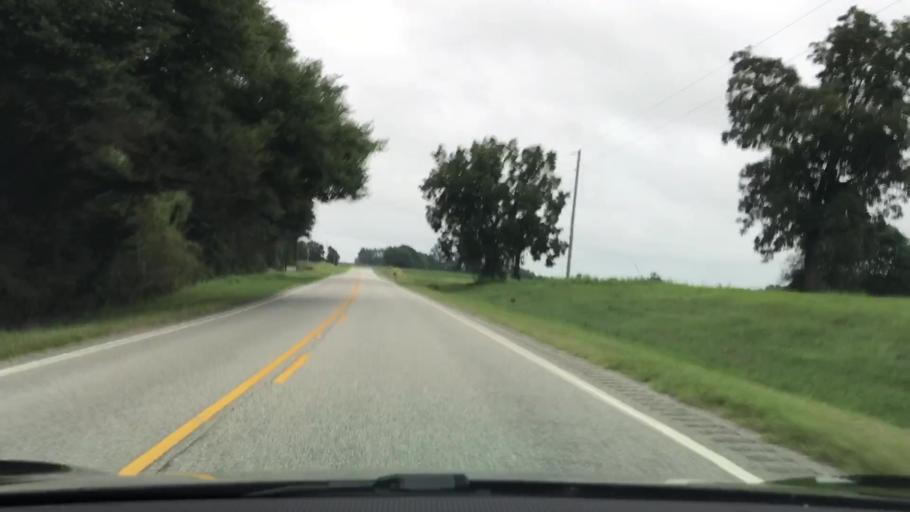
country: US
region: Alabama
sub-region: Coffee County
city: Elba
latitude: 31.3149
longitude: -86.1342
